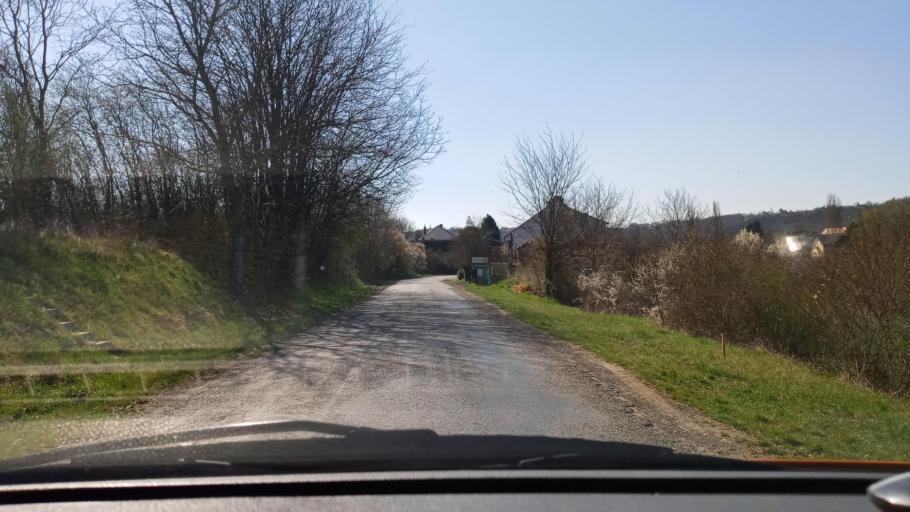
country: HU
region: Baranya
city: Kozarmisleny
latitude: 46.0377
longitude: 18.3872
